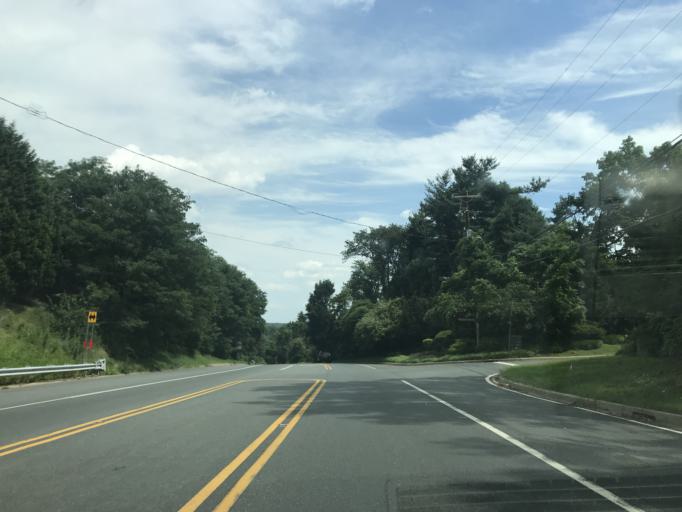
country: US
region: Delaware
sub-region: New Castle County
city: Hockessin
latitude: 39.7654
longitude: -75.6529
